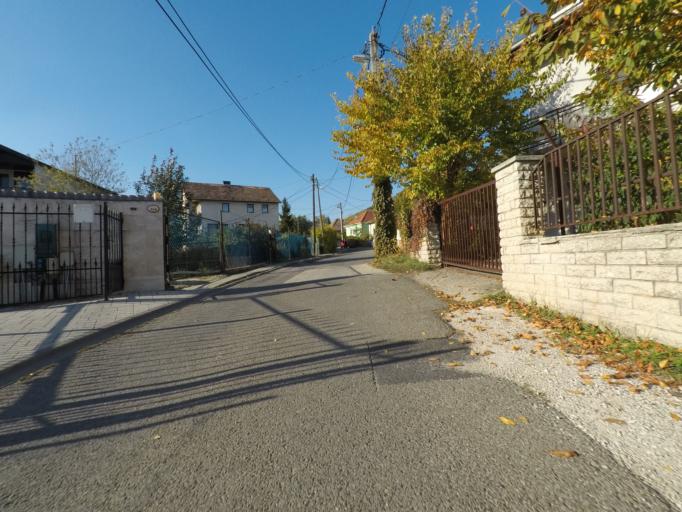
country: HU
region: Pest
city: Nagykovacsi
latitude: 47.6523
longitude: 19.0048
